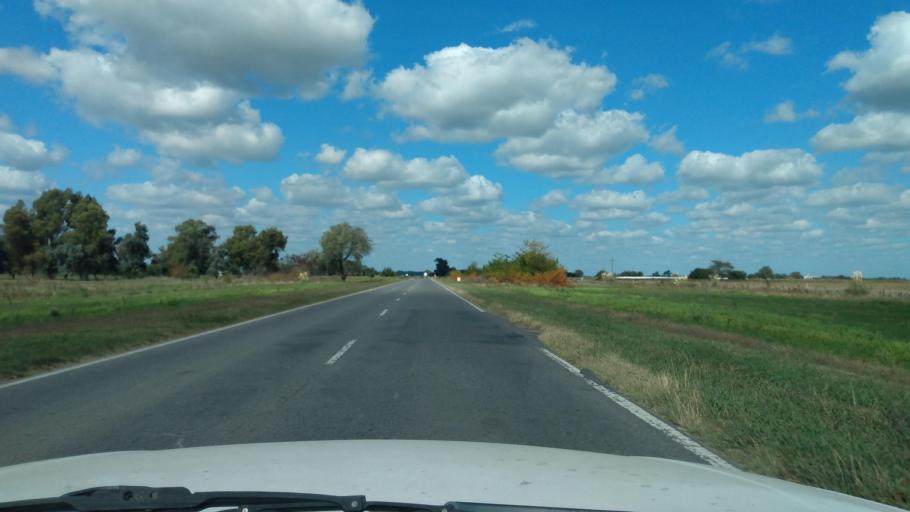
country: AR
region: Buenos Aires
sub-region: Partido de Navarro
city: Navarro
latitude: -34.9500
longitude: -59.3200
